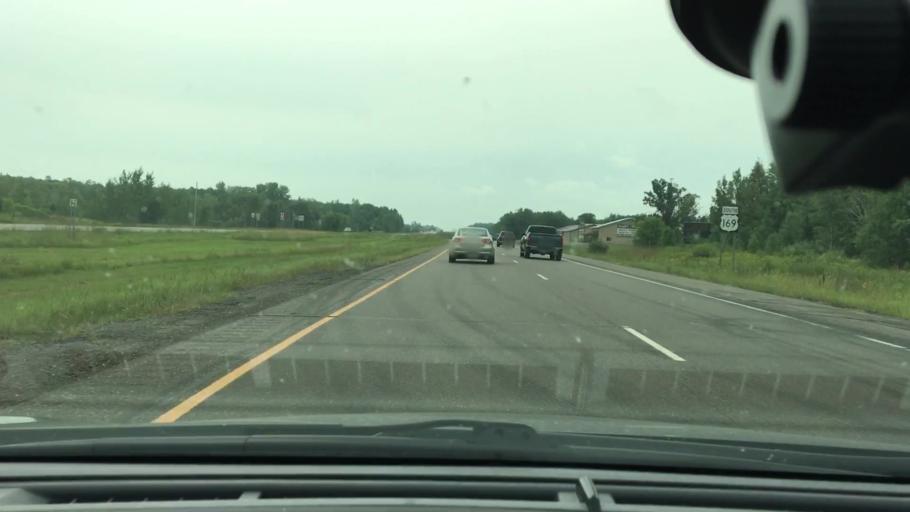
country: US
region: Minnesota
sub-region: Mille Lacs County
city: Vineland
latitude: 46.0546
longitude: -93.6628
